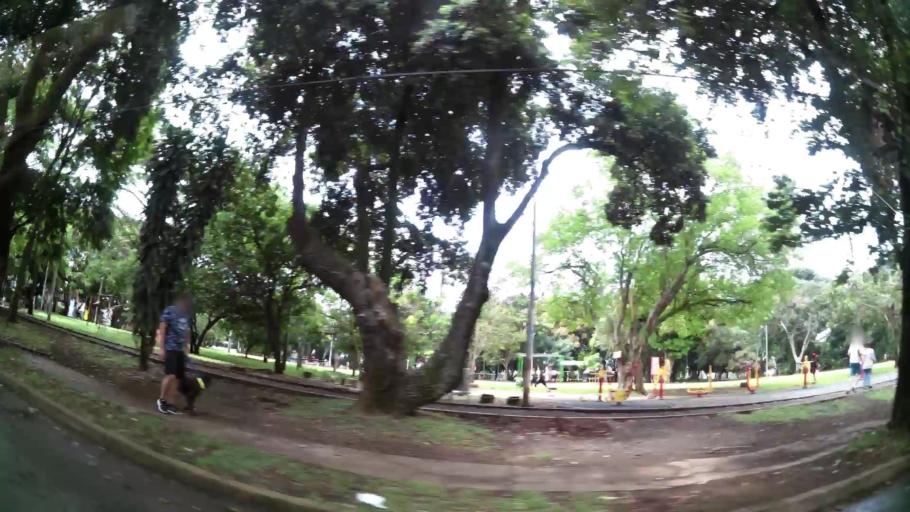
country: CO
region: Valle del Cauca
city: Cali
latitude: 3.3892
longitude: -76.5411
